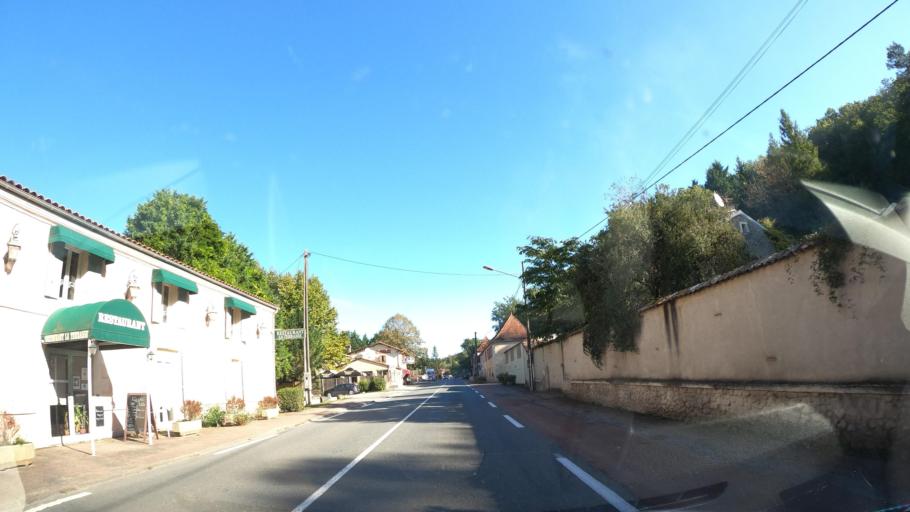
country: FR
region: Aquitaine
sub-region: Departement de la Dordogne
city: Lembras
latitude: 44.9337
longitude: 0.5624
